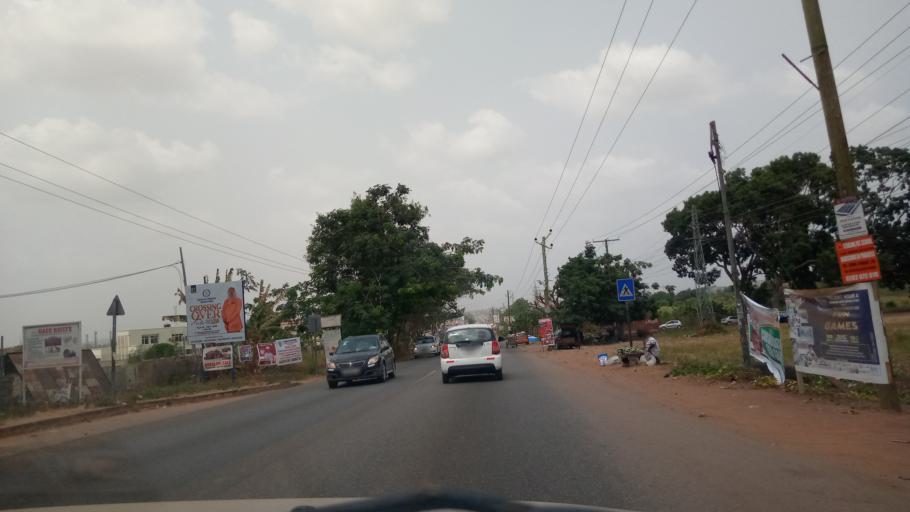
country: GH
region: Greater Accra
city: Dome
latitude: 5.6677
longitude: -0.2322
